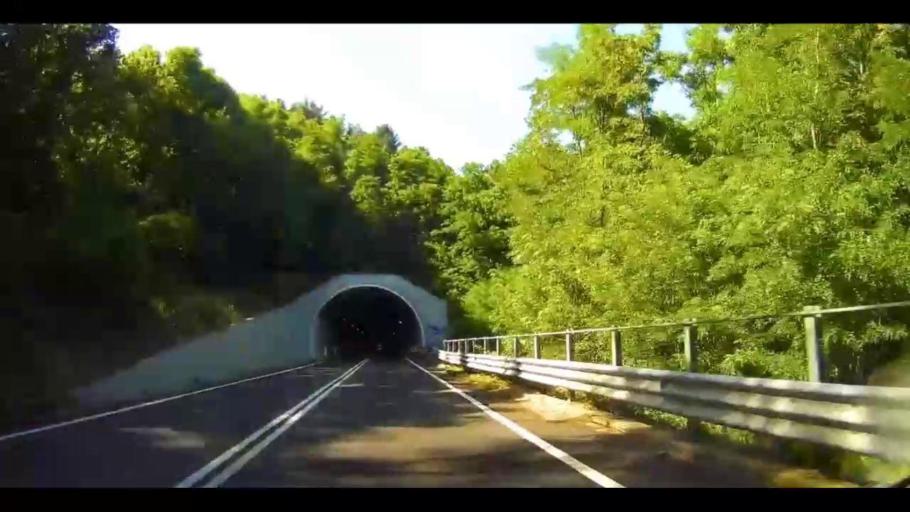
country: IT
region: Calabria
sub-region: Provincia di Cosenza
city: Spezzano della Sila
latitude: 39.3008
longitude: 16.3558
